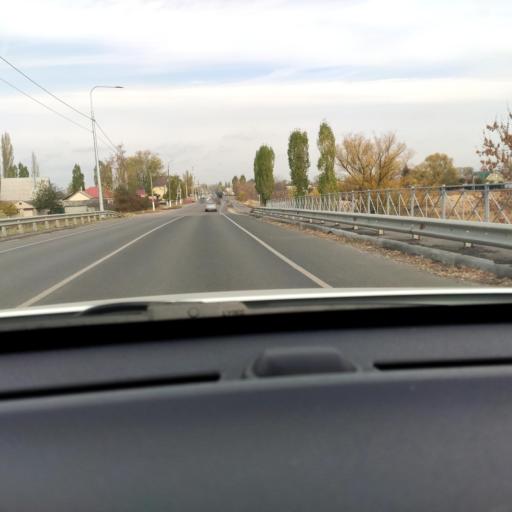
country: RU
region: Voronezj
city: Novaya Usman'
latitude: 51.6265
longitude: 39.3991
